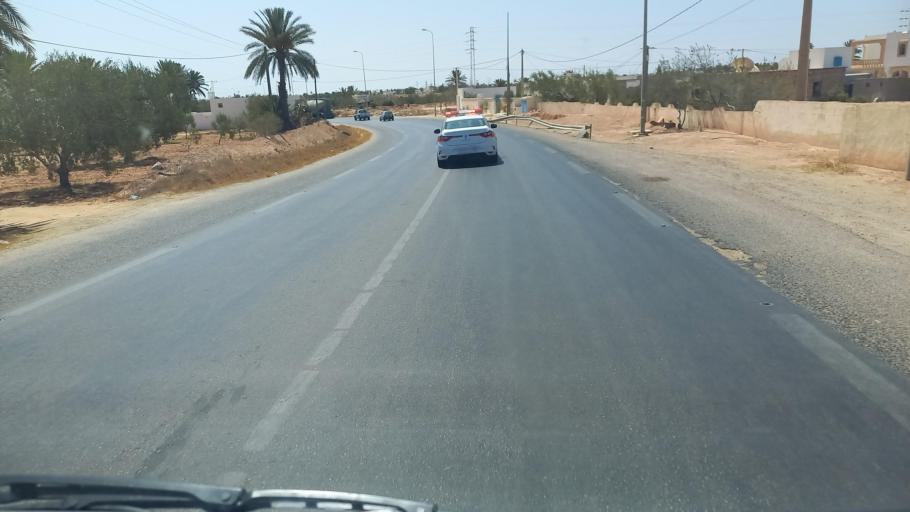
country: TN
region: Madanin
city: Houmt Souk
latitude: 33.7842
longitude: 10.8877
